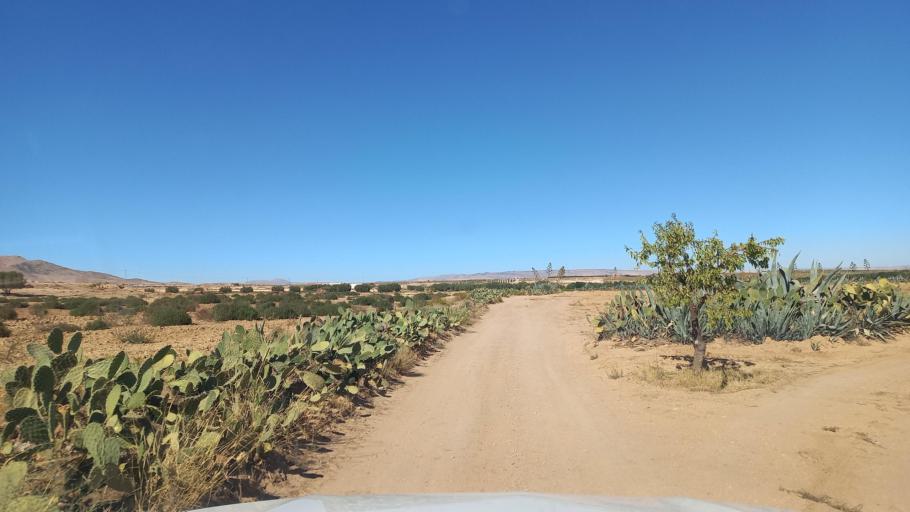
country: TN
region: Al Qasrayn
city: Sbiba
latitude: 35.4015
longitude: 9.0865
